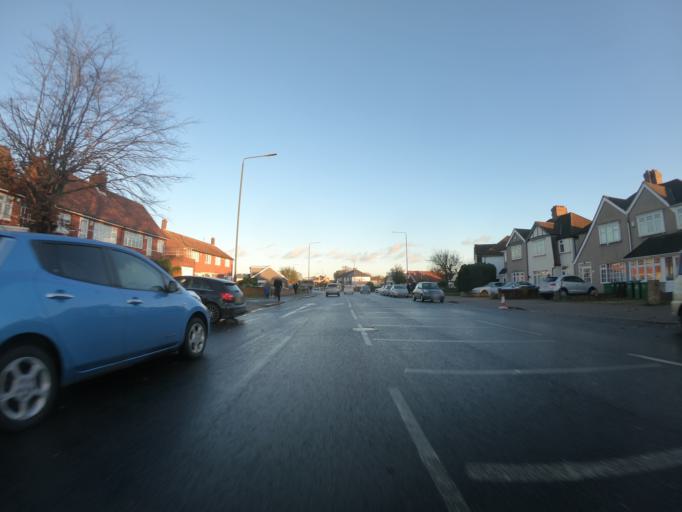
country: GB
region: England
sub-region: Greater London
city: Bexleyheath
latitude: 51.4815
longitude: 0.1310
